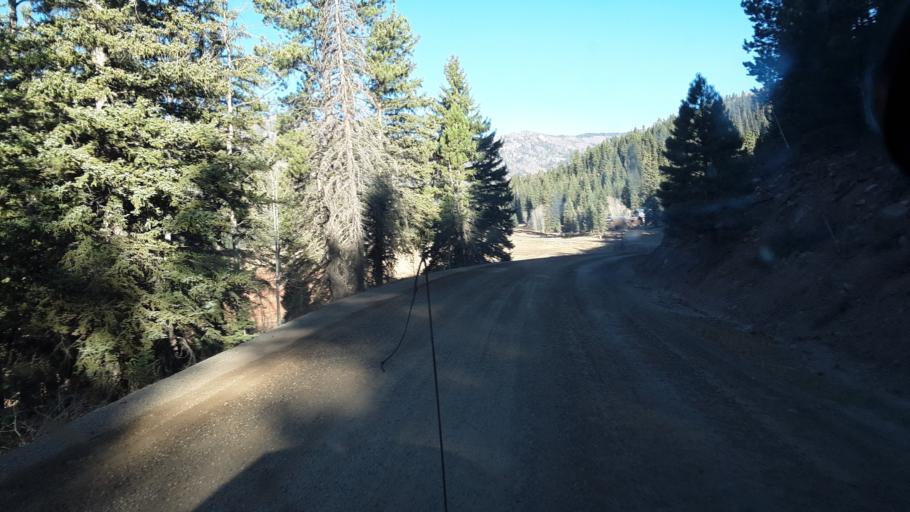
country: US
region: Colorado
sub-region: La Plata County
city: Bayfield
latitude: 37.4195
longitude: -107.6663
